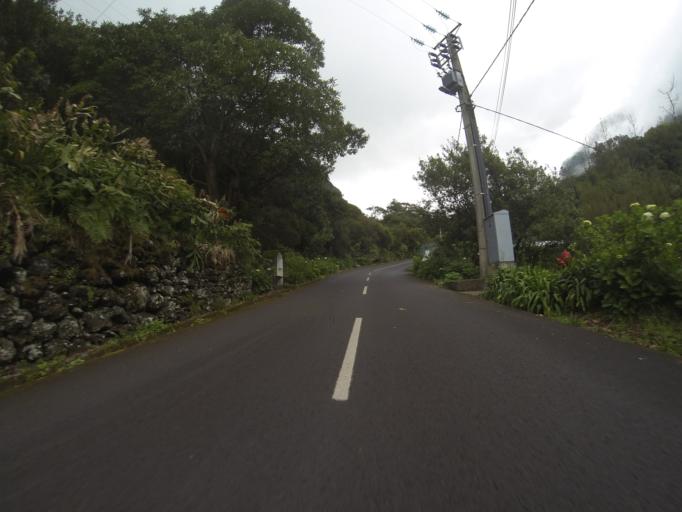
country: PT
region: Madeira
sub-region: Porto Moniz
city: Porto Moniz
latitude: 32.8135
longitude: -17.1117
